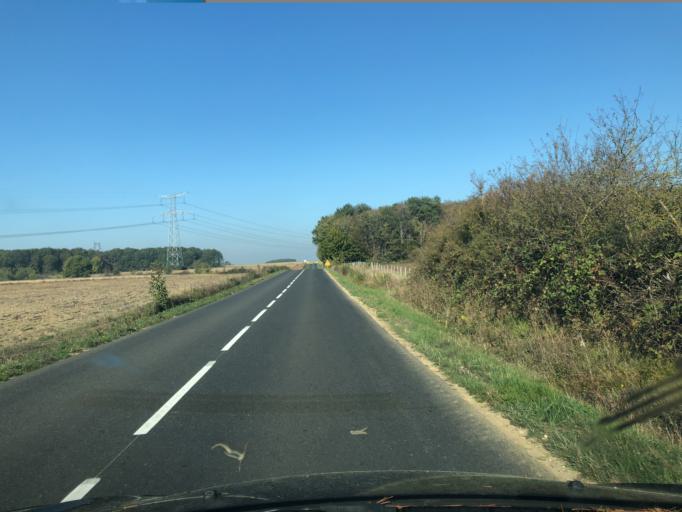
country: FR
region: Centre
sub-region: Departement d'Indre-et-Loire
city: Rouziers-de-Touraine
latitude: 47.5295
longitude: 0.6400
